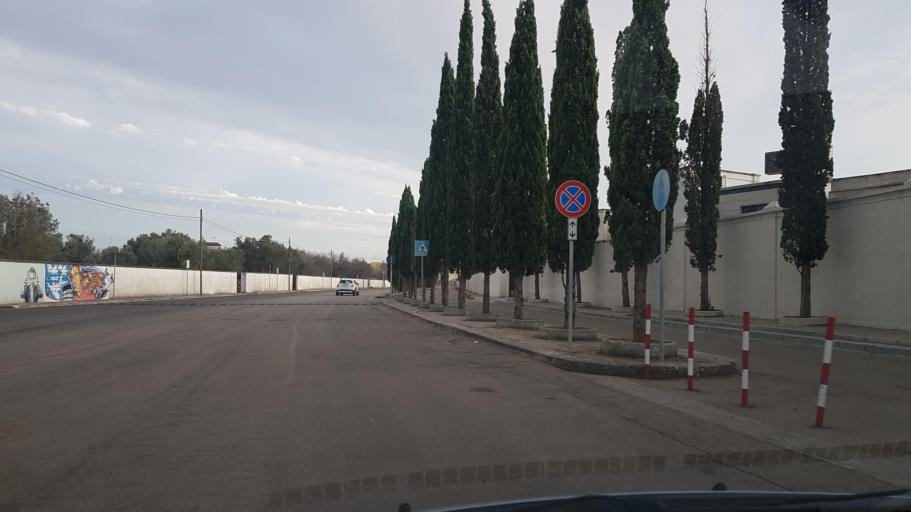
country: IT
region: Apulia
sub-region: Provincia di Lecce
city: Surbo
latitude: 40.4044
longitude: 18.1279
